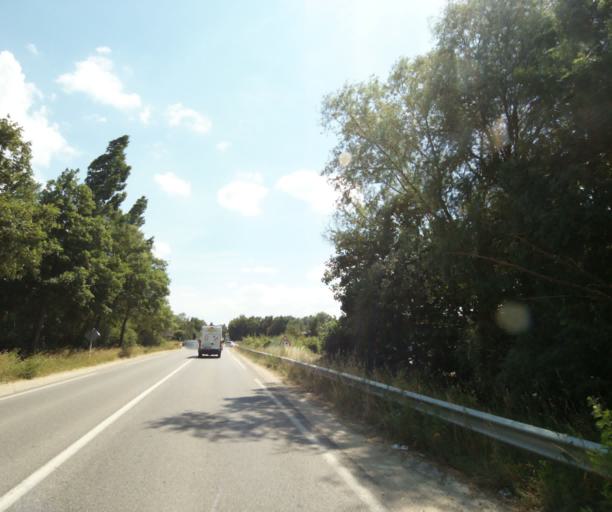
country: FR
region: Lorraine
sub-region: Departement de Meurthe-et-Moselle
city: Luneville
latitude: 48.5781
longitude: 6.4815
